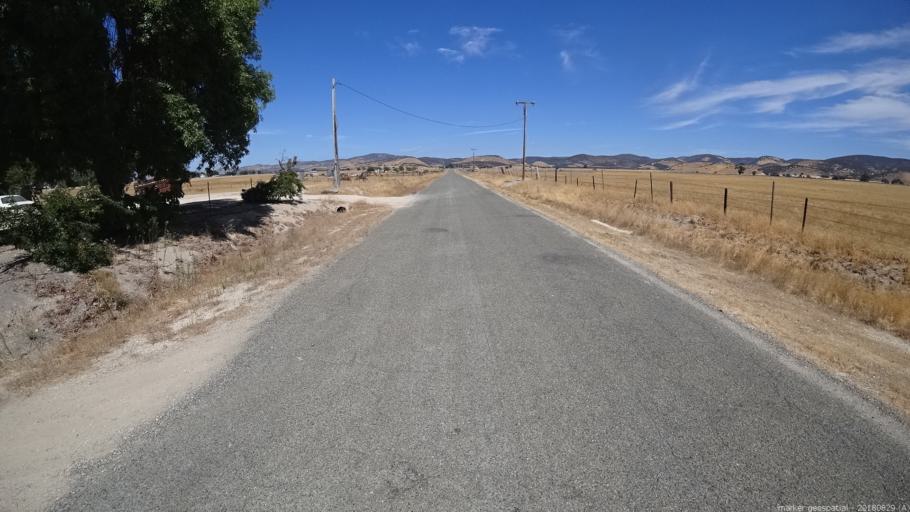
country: US
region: California
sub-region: San Luis Obispo County
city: Lake Nacimiento
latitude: 35.9326
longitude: -121.0642
